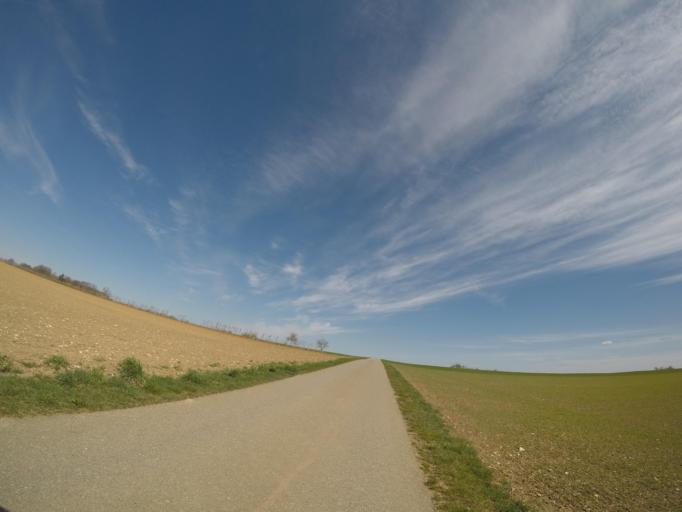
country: DE
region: Baden-Wuerttemberg
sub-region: Tuebingen Region
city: Mehrstetten
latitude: 48.3407
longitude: 9.5546
